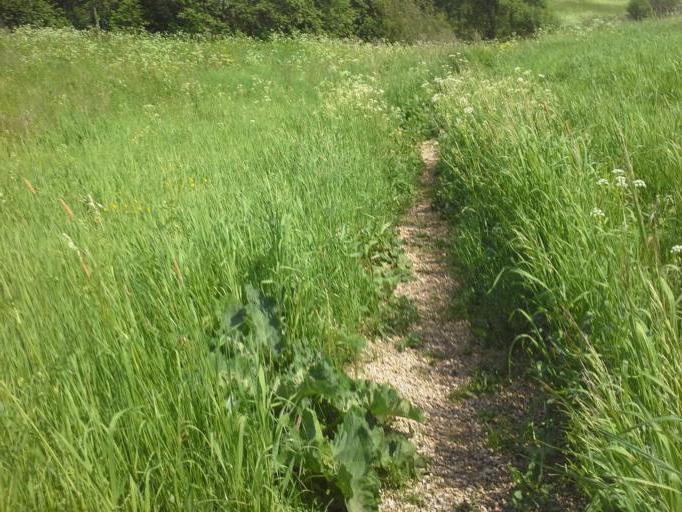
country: RU
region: Moskovskaya
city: Filimonki
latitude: 55.5792
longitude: 37.3438
